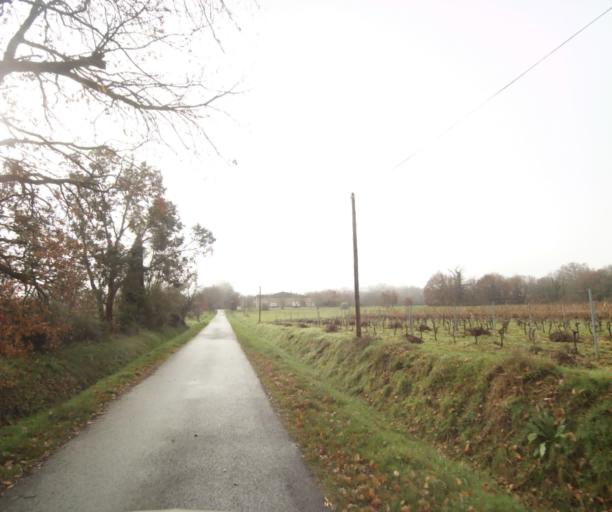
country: FR
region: Midi-Pyrenees
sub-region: Departement de la Haute-Garonne
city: Villemur-sur-Tarn
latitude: 43.8435
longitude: 1.4950
